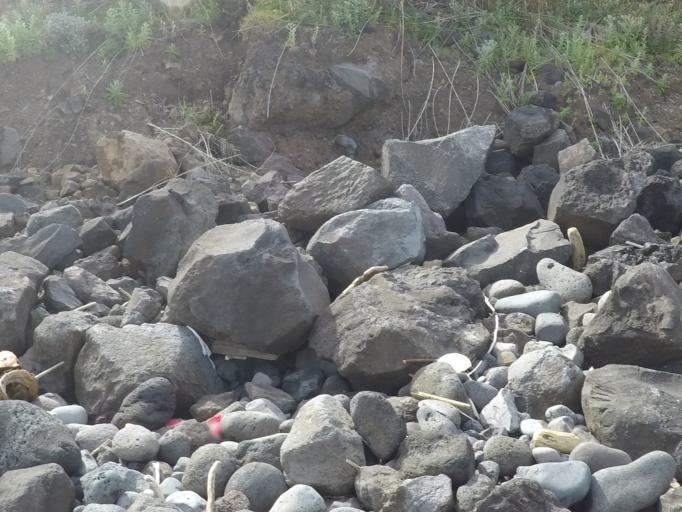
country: PT
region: Madeira
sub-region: Sao Vicente
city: Sao Vicente
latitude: 32.8229
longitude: -17.0022
